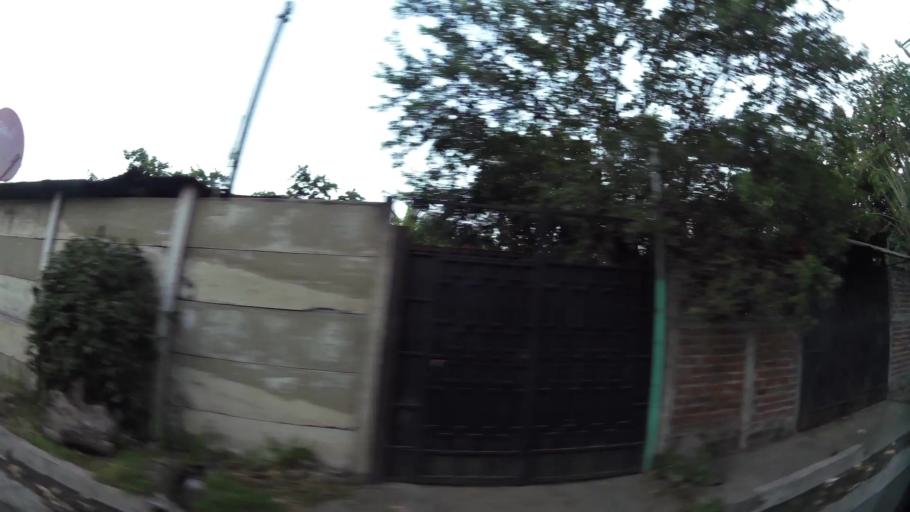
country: SV
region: La Libertad
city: Santa Tecla
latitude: 13.7333
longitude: -89.3776
